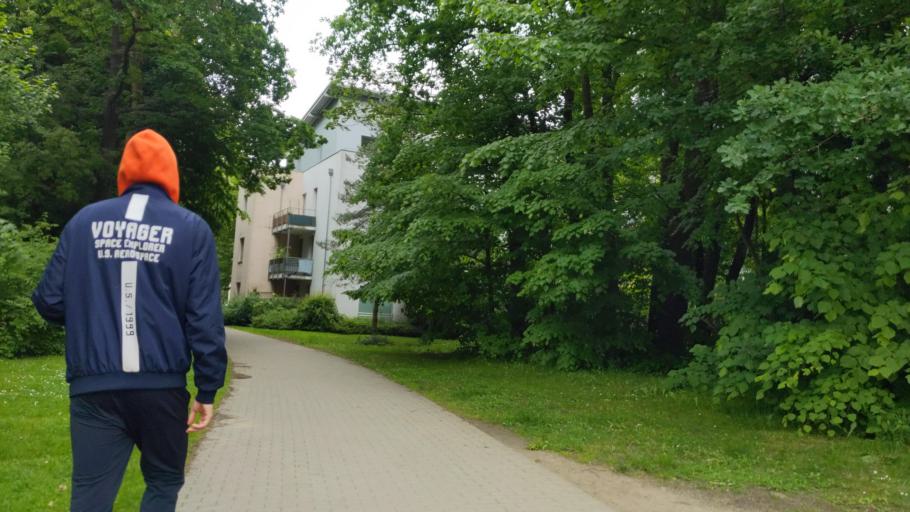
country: DE
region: Schleswig-Holstein
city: Luebeck
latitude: 53.8933
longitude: 10.6862
